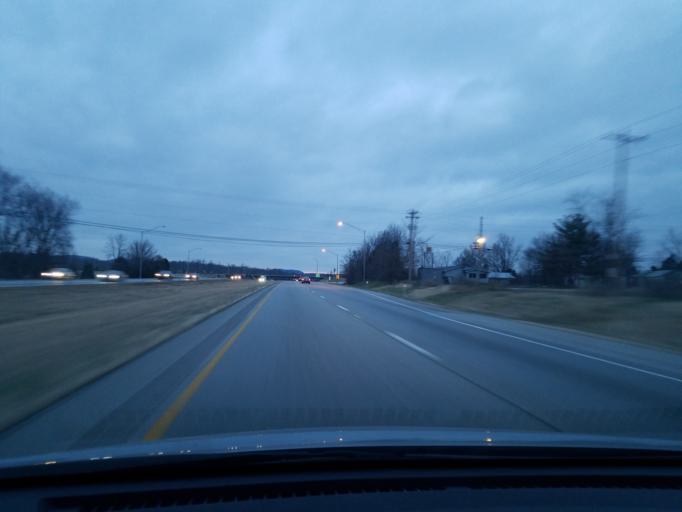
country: US
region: Indiana
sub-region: Clark County
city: Henryville
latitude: 38.5362
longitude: -85.7764
